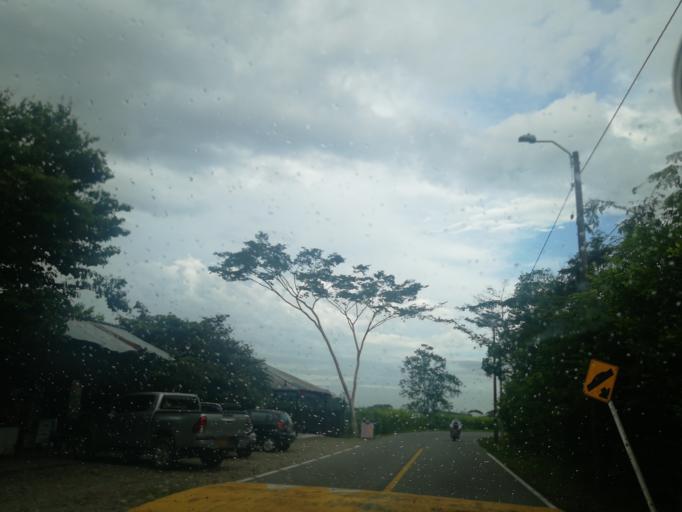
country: CO
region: Meta
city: Acacias
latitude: 3.9859
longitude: -73.7270
